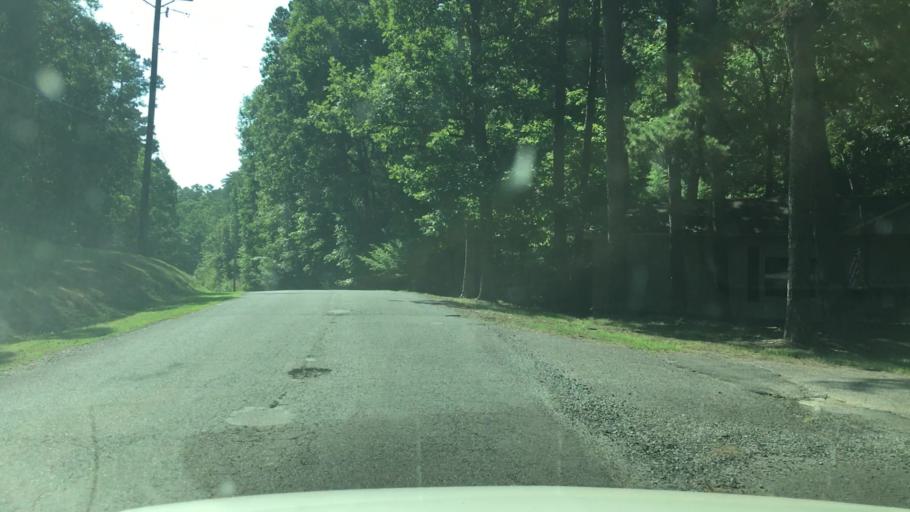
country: US
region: Arkansas
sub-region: Garland County
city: Piney
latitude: 34.5440
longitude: -93.3603
